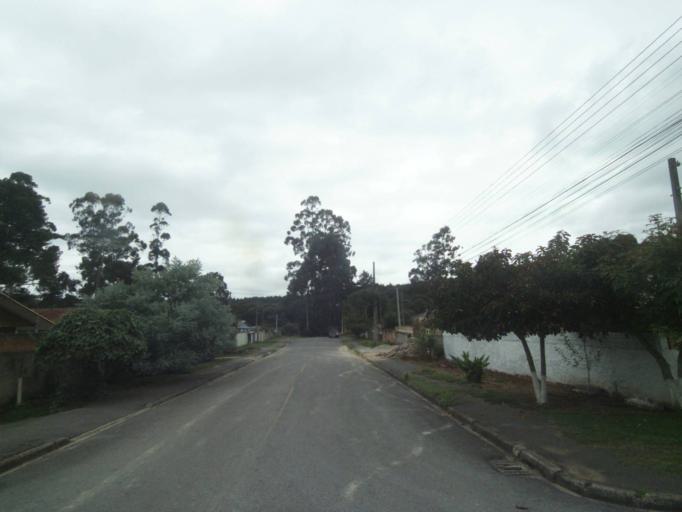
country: BR
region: Parana
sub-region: Quatro Barras
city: Quatro Barras
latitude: -25.3501
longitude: -49.1065
